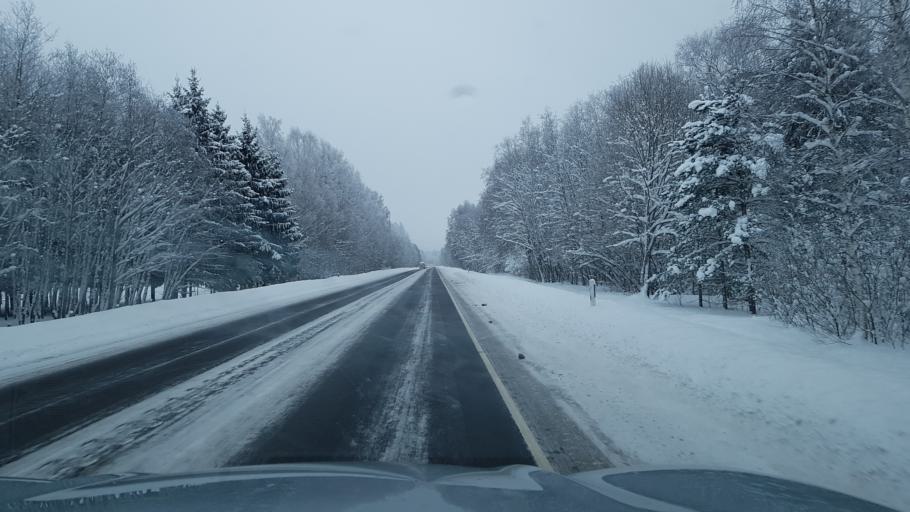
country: EE
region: Ida-Virumaa
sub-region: Johvi vald
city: Johvi
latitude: 59.3015
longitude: 27.3954
